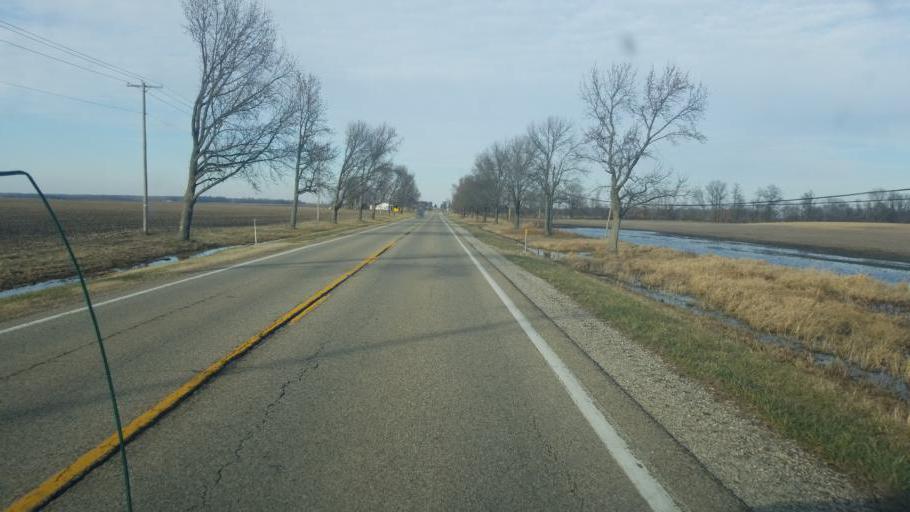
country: US
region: Illinois
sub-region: Lawrence County
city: Bridgeport
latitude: 38.5941
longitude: -87.6943
